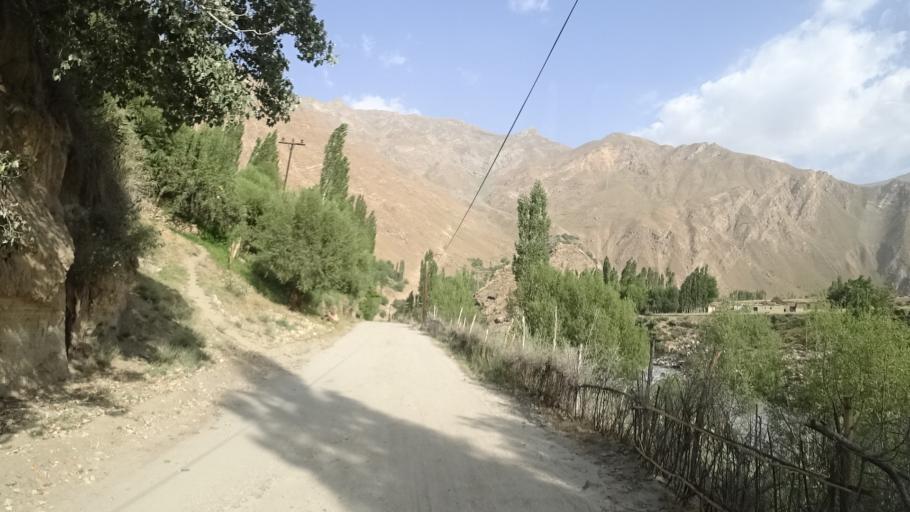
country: TJ
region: Gorno-Badakhshan
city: Khorugh
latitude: 37.3188
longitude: 71.5013
